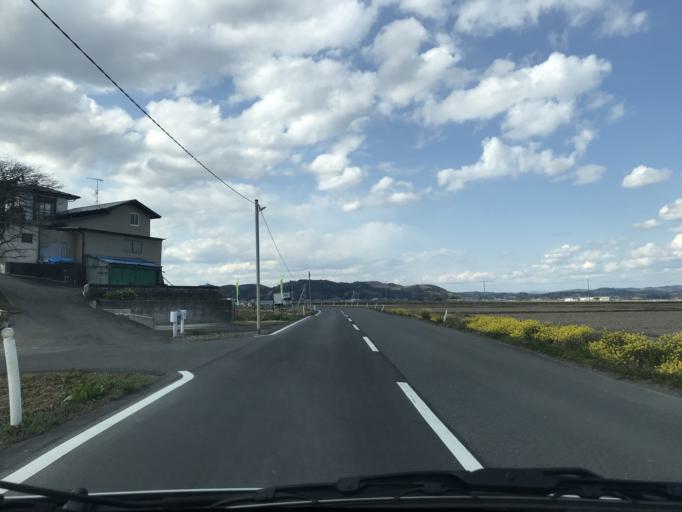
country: JP
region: Miyagi
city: Wakuya
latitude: 38.7257
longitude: 141.2329
